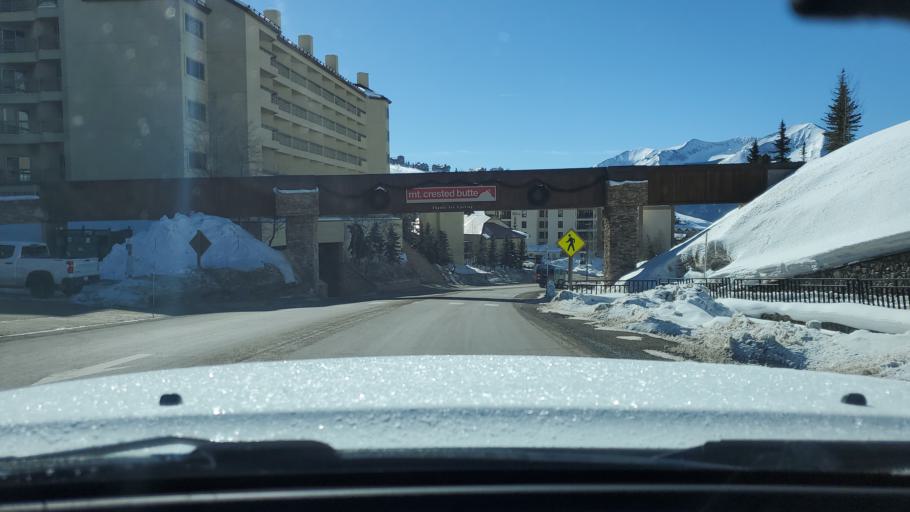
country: US
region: Colorado
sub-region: Gunnison County
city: Crested Butte
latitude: 38.8999
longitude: -106.9674
